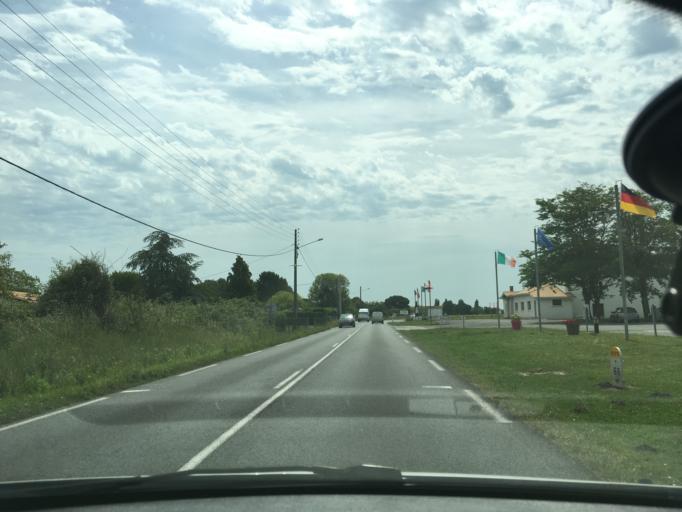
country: FR
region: Aquitaine
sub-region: Departement de la Gironde
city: Gaillan-en-Medoc
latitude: 45.3273
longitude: -0.9657
